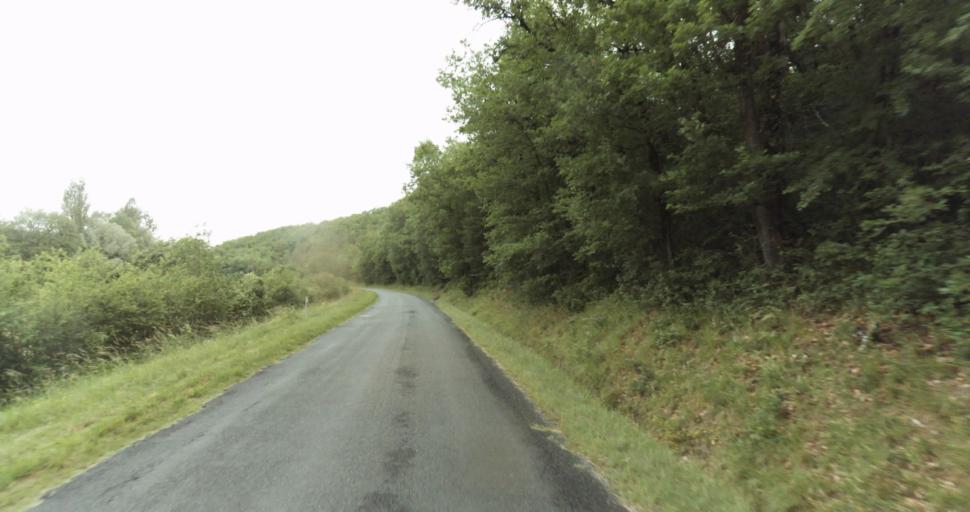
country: FR
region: Aquitaine
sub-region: Departement de la Dordogne
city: Beaumont-du-Perigord
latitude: 44.7544
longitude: 0.8161
